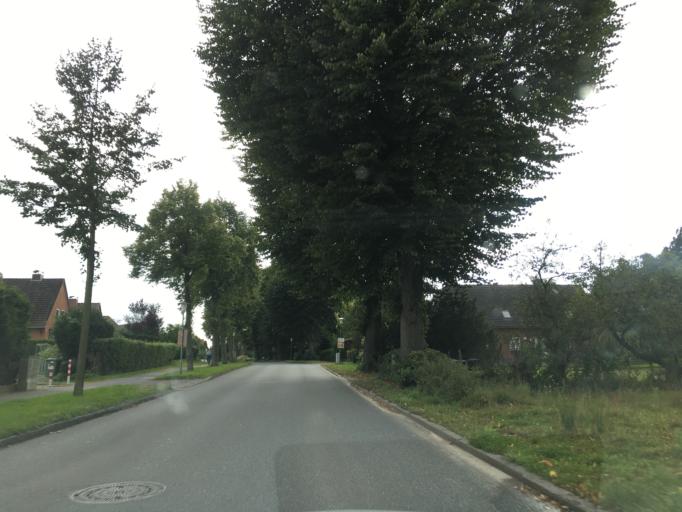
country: DE
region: Schleswig-Holstein
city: Brodersdorf
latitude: 54.3765
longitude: 10.2299
